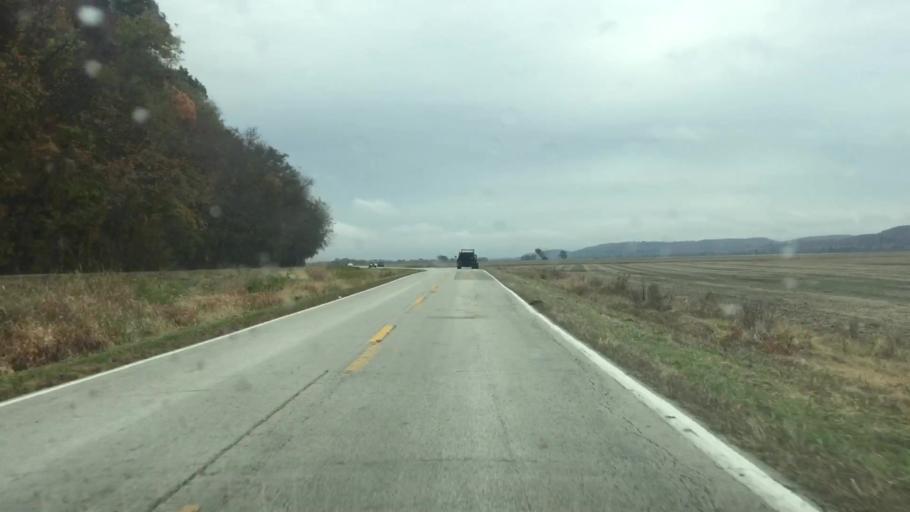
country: US
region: Missouri
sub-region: Gasconade County
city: Hermann
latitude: 38.7035
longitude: -91.5642
